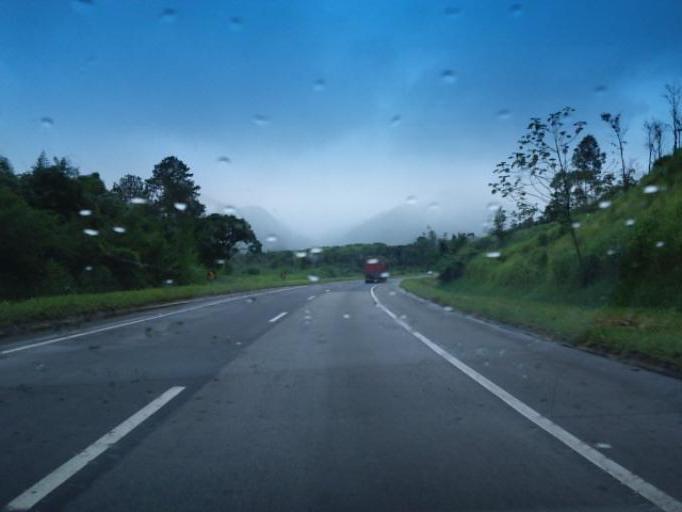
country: BR
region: Sao Paulo
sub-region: Cajati
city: Cajati
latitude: -24.7799
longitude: -48.1944
